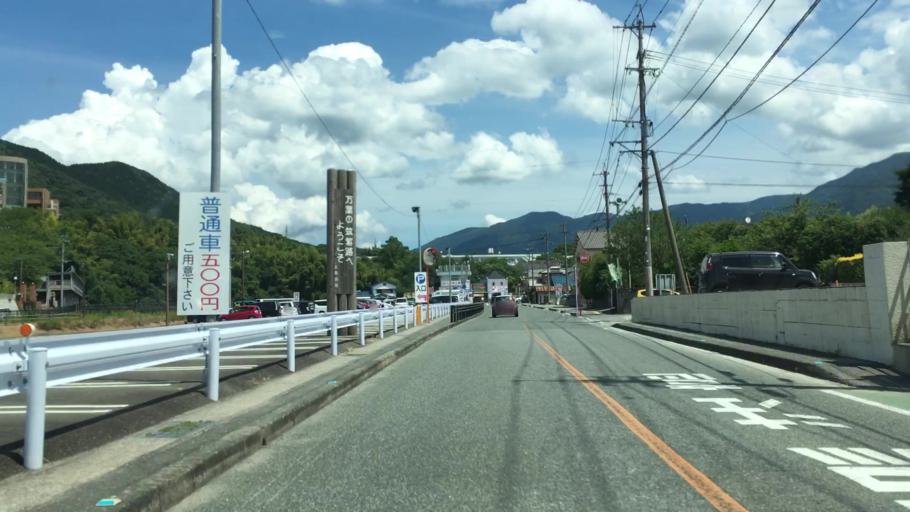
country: JP
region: Fukuoka
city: Dazaifu
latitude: 33.5175
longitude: 130.5280
